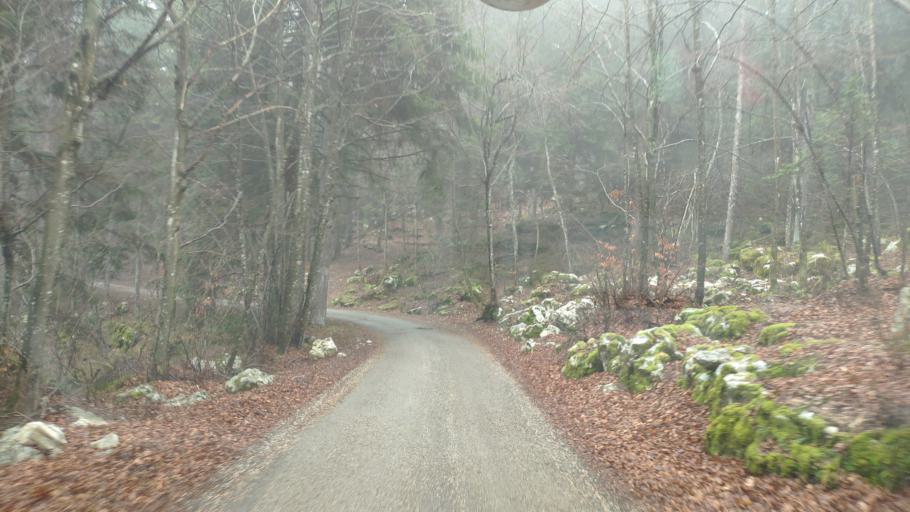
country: IT
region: Veneto
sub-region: Provincia di Vicenza
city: Rotzo
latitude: 45.8265
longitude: 11.4010
